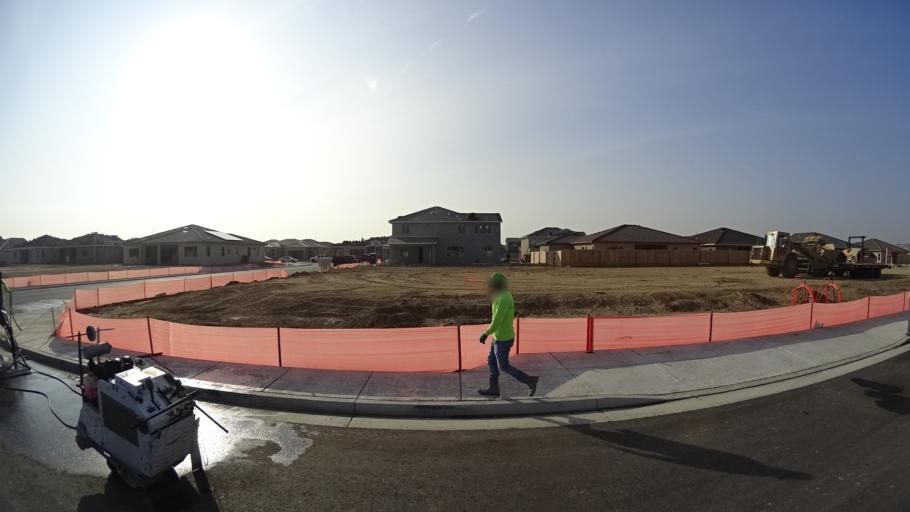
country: US
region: California
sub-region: Kern County
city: Greenacres
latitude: 35.4337
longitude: -119.1030
